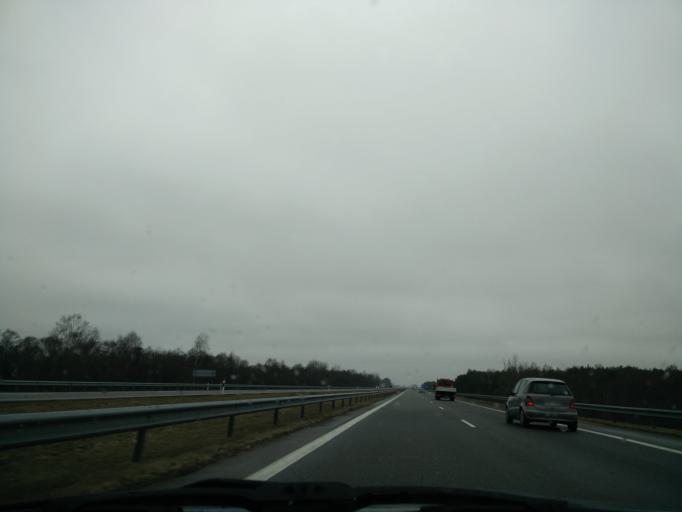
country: LT
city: Kelme
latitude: 55.3945
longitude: 22.8746
